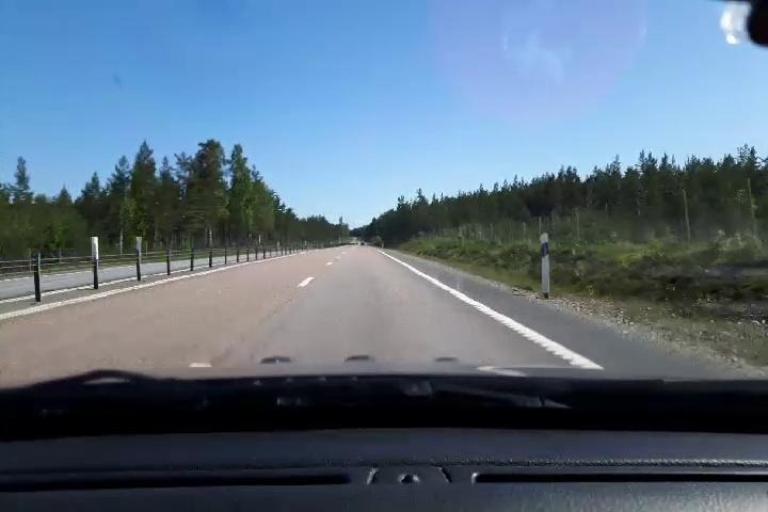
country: SE
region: Gaevleborg
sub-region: Gavle Kommun
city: Norrsundet
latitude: 60.9797
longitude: 17.0180
